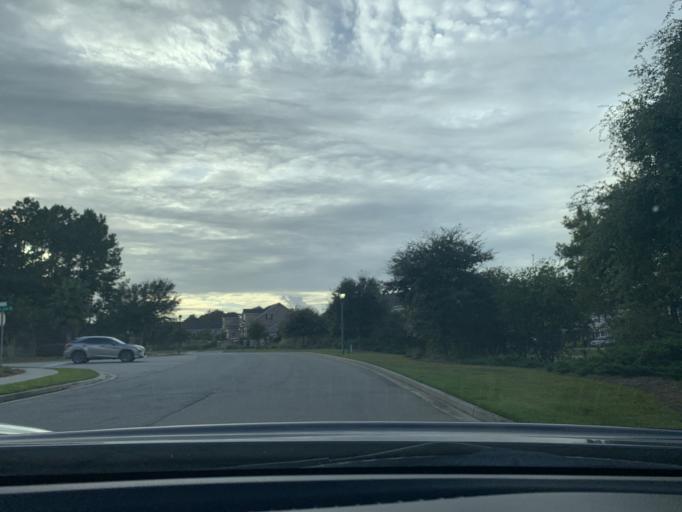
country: US
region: Georgia
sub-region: Chatham County
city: Pooler
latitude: 32.0752
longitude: -81.2619
